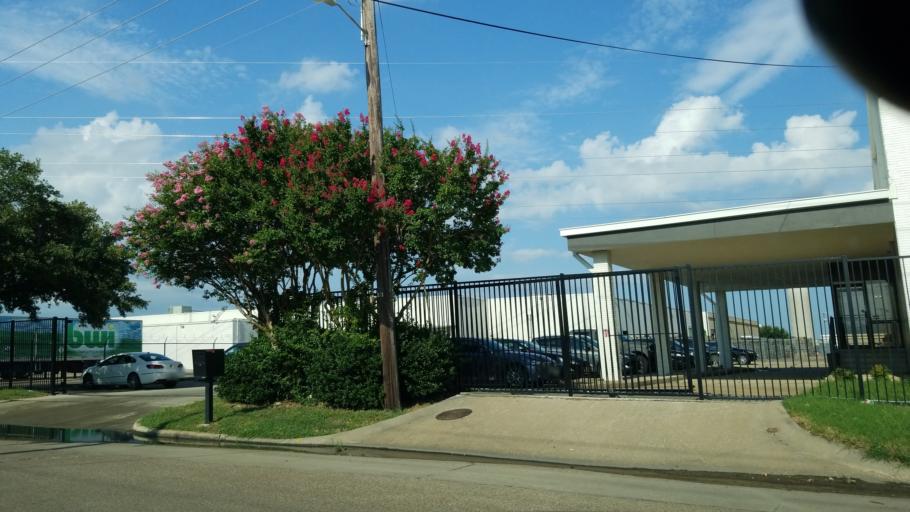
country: US
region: Texas
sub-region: Dallas County
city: Carrollton
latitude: 32.9495
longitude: -96.9115
